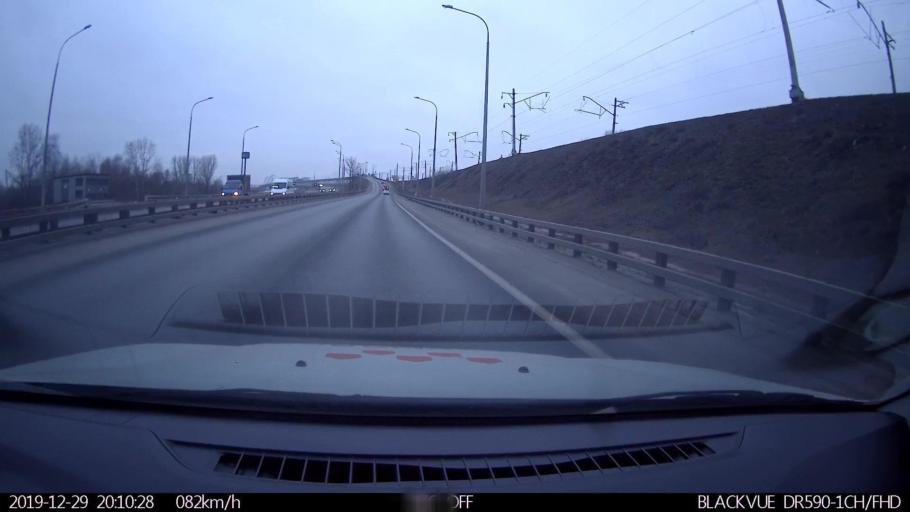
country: RU
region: Nizjnij Novgorod
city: Neklyudovo
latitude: 56.3652
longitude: 43.9360
